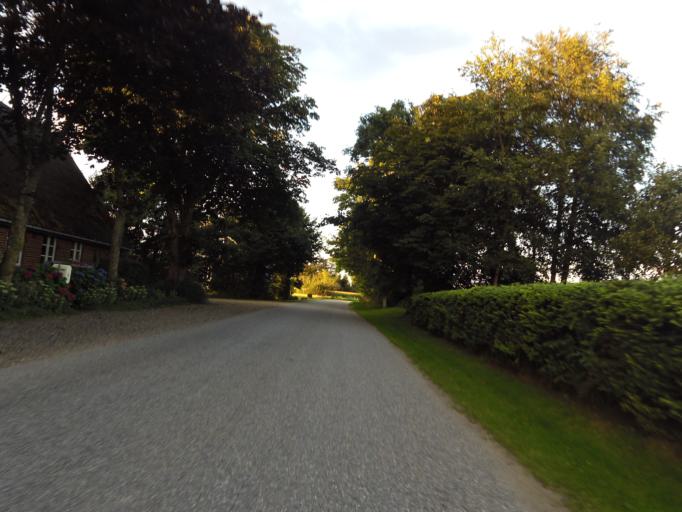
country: DK
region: South Denmark
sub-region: Esbjerg Kommune
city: Ribe
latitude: 55.2476
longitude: 8.8967
